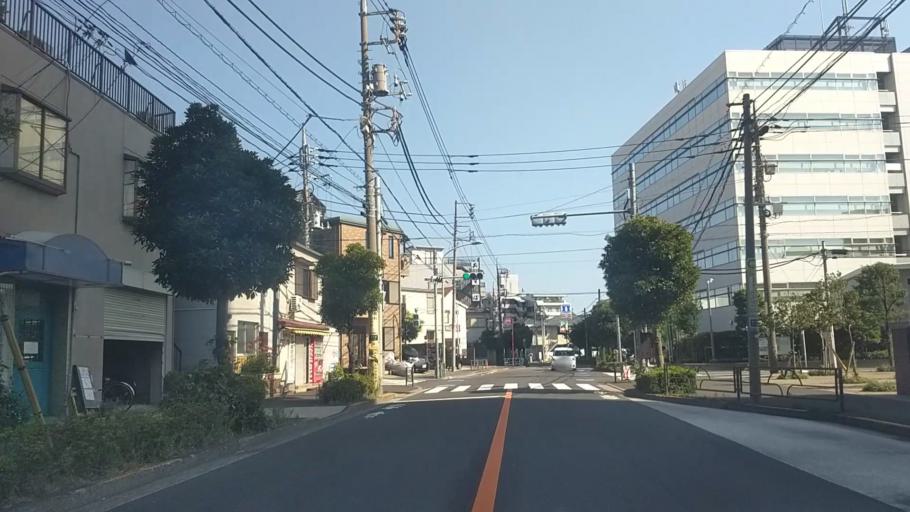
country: JP
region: Kanagawa
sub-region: Kawasaki-shi
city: Kawasaki
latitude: 35.5433
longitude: 139.7048
